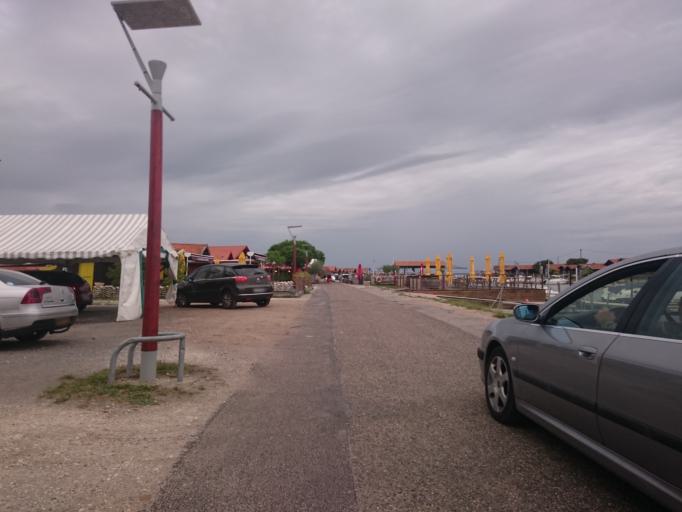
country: FR
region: Aquitaine
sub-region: Departement de la Gironde
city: Gujan-Mestras
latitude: 44.6422
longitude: -1.0730
